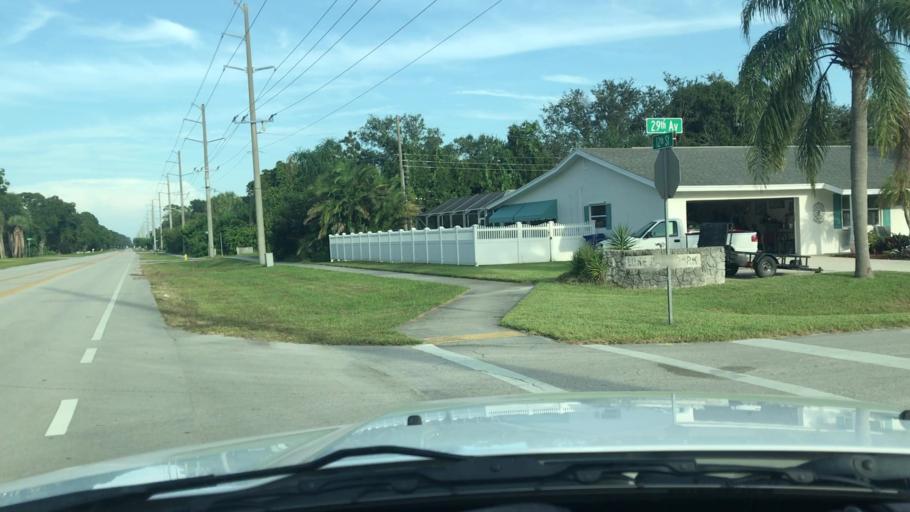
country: US
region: Florida
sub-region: Indian River County
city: Vero Beach South
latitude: 27.6240
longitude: -80.4152
